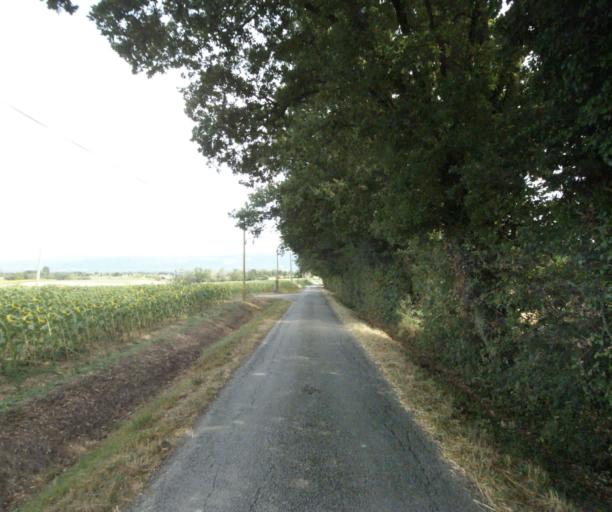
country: FR
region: Midi-Pyrenees
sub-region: Departement du Tarn
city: Puylaurens
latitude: 43.5396
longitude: 2.0501
